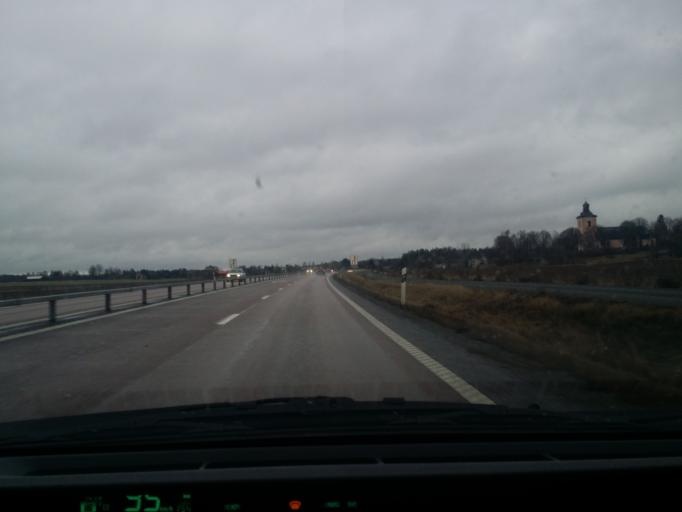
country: SE
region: Vaestmanland
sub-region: Sala Kommun
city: Sala
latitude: 59.8667
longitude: 16.5412
